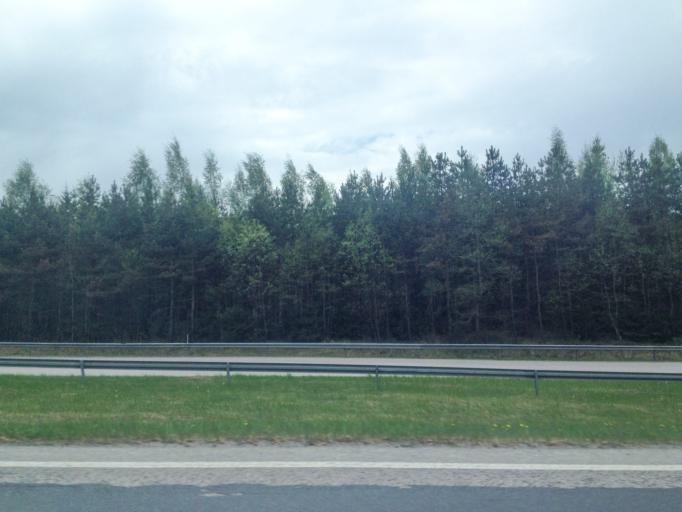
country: FI
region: Uusimaa
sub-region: Helsinki
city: Hyvinge
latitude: 60.5634
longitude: 24.8218
